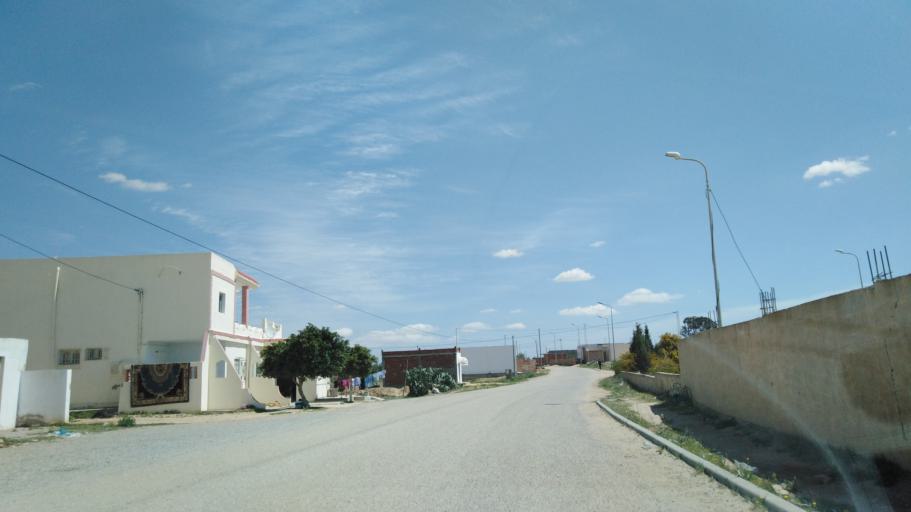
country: TN
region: Safaqis
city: Sfax
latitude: 34.7413
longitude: 10.5413
